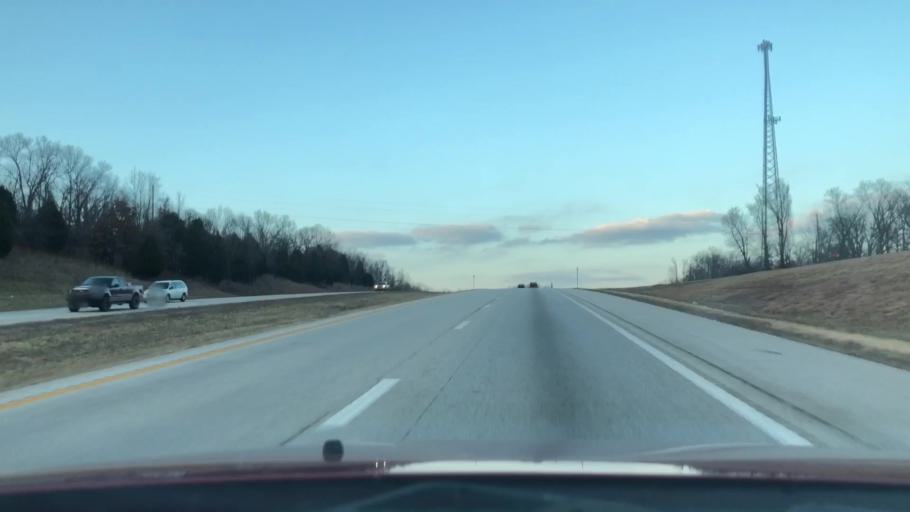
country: US
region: Missouri
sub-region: Christian County
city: Ozark
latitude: 36.9164
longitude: -93.2437
